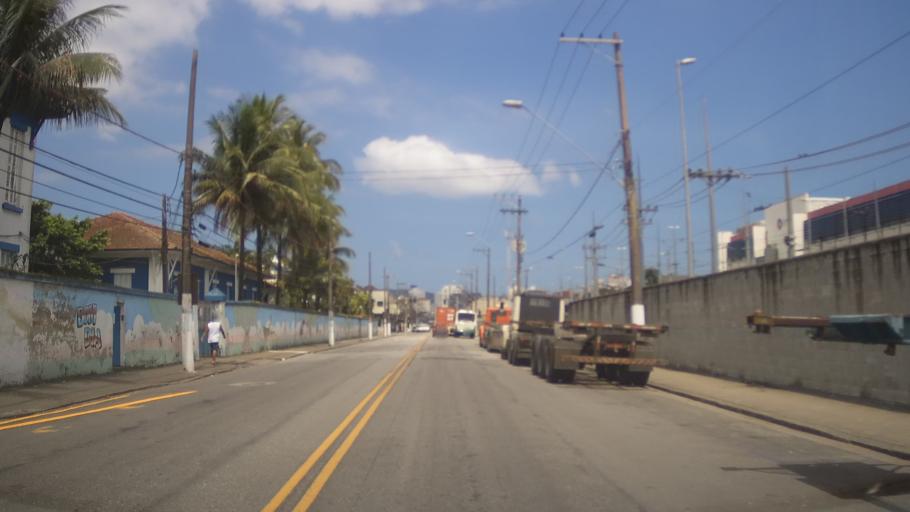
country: BR
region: Sao Paulo
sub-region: Santos
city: Santos
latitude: -23.9551
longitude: -46.3132
